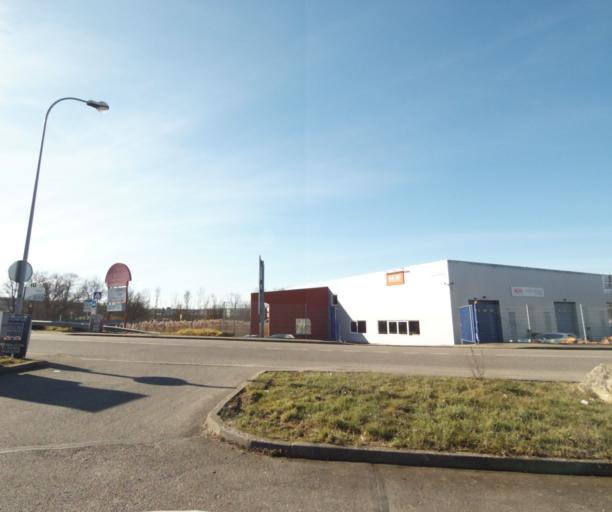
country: FR
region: Lorraine
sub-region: Departement de Meurthe-et-Moselle
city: Richardmenil
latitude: 48.6097
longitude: 6.1732
